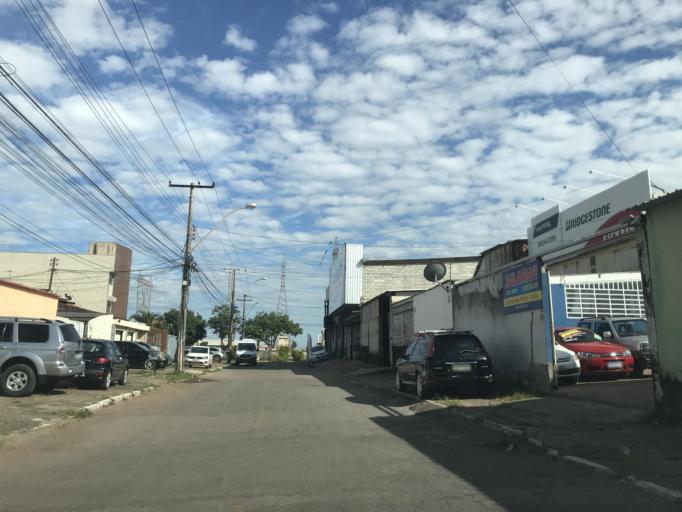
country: BR
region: Federal District
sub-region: Brasilia
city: Brasilia
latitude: -15.8538
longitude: -48.0405
